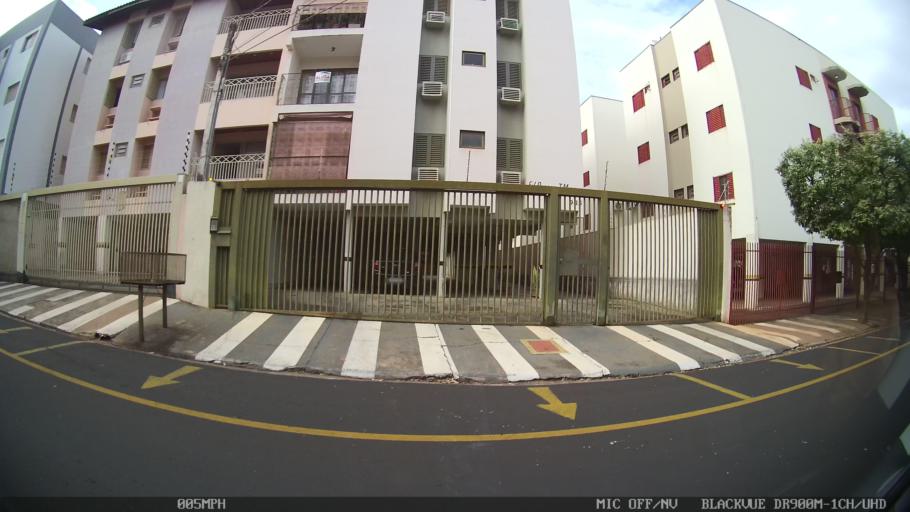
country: BR
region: Sao Paulo
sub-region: Sao Jose Do Rio Preto
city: Sao Jose do Rio Preto
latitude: -20.8304
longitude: -49.3821
